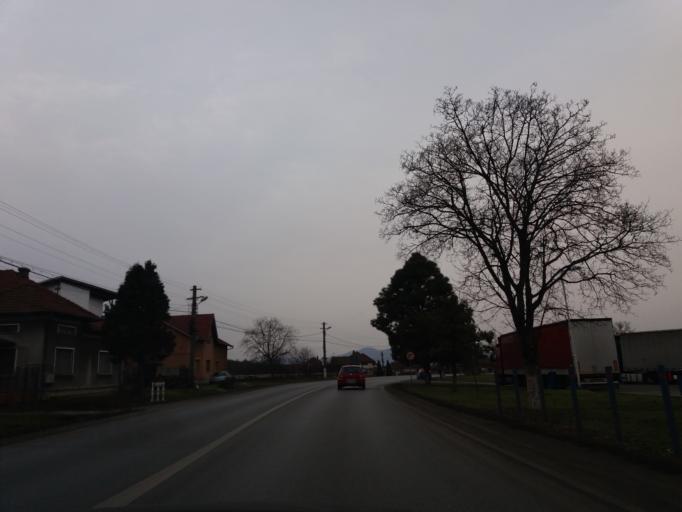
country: RO
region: Hunedoara
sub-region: Oras Simeria
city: Simeria
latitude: 45.8451
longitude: 23.0068
